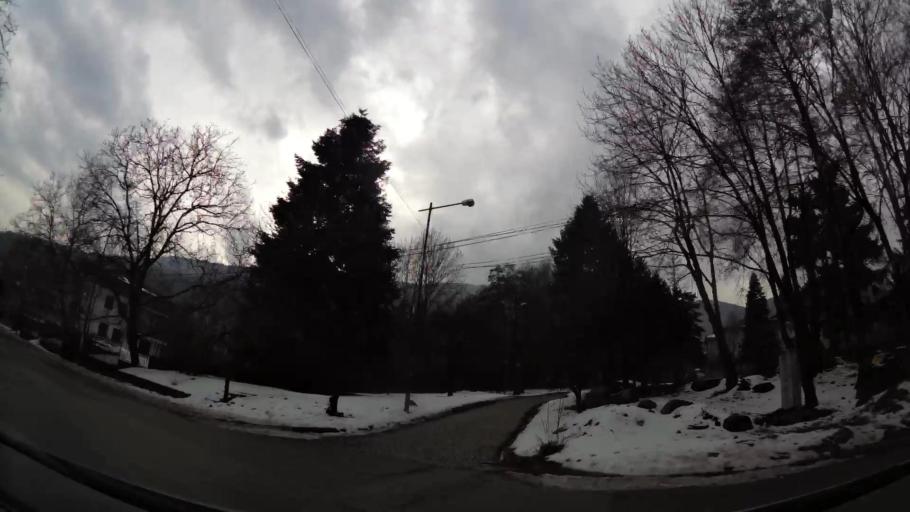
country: BG
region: Sofia-Capital
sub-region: Stolichna Obshtina
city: Sofia
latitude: 42.6456
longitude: 23.2679
